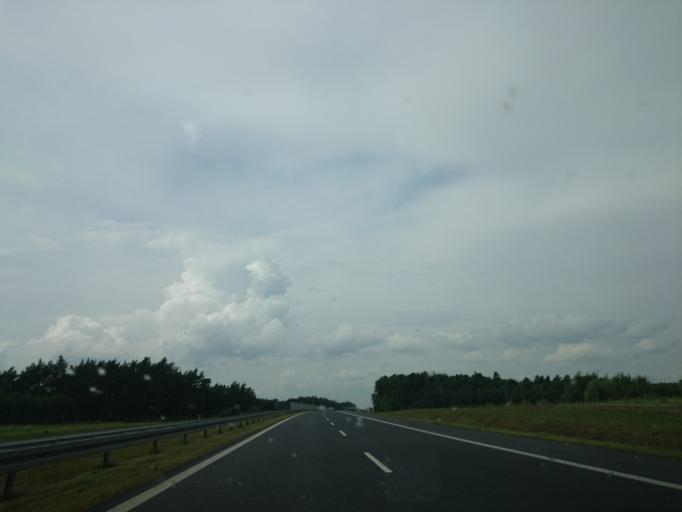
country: PL
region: West Pomeranian Voivodeship
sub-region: Powiat pyrzycki
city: Lipiany
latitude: 52.9614
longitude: 14.9247
